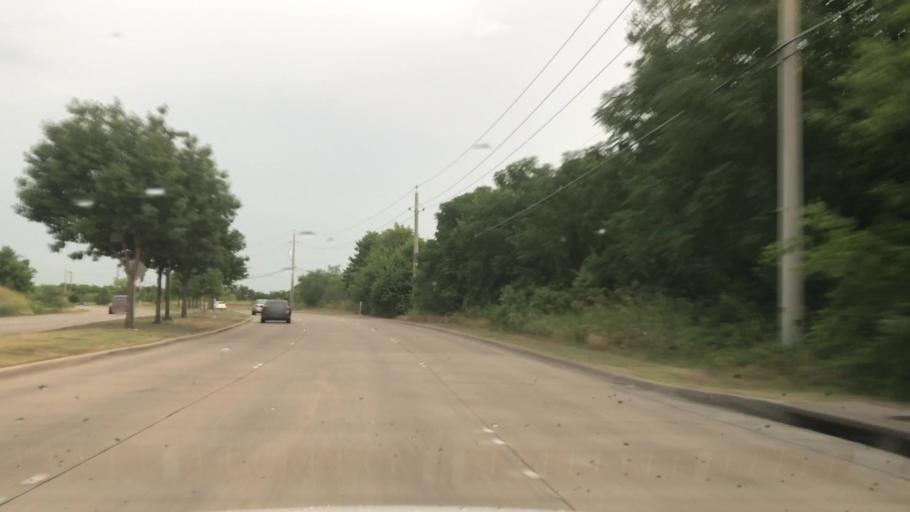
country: US
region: Texas
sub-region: Dallas County
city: Mesquite
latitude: 32.7382
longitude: -96.5725
